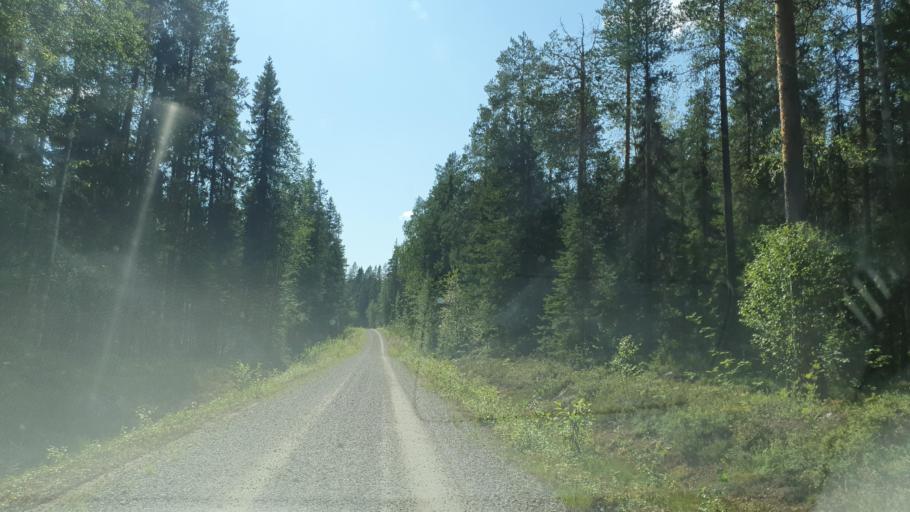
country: FI
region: Kainuu
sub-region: Kehys-Kainuu
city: Kuhmo
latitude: 63.9762
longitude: 29.5410
